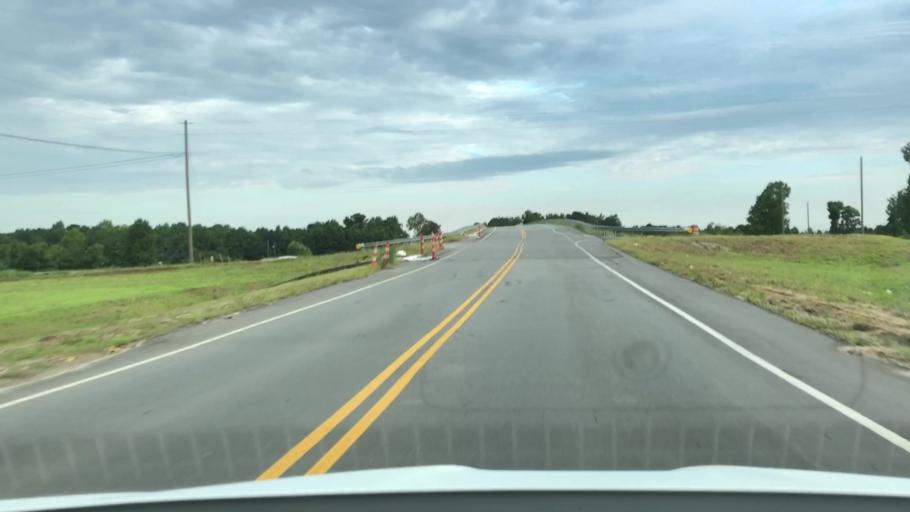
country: US
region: North Carolina
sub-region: Jones County
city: Maysville
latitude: 34.9103
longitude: -77.2366
